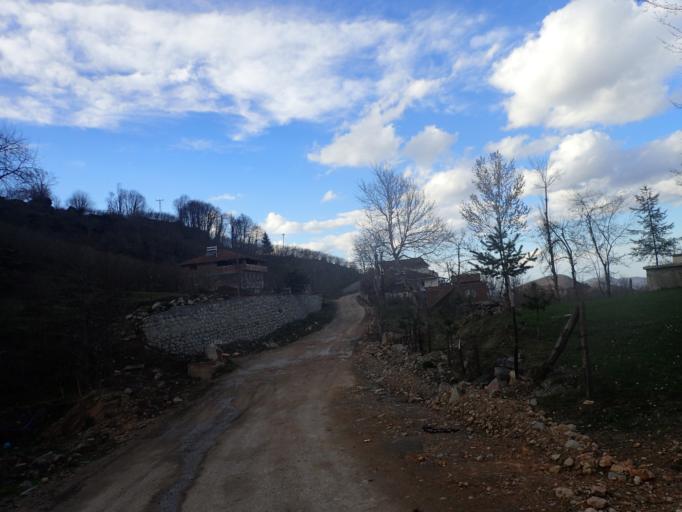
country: TR
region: Ordu
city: Kumru
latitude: 40.9294
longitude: 37.2406
